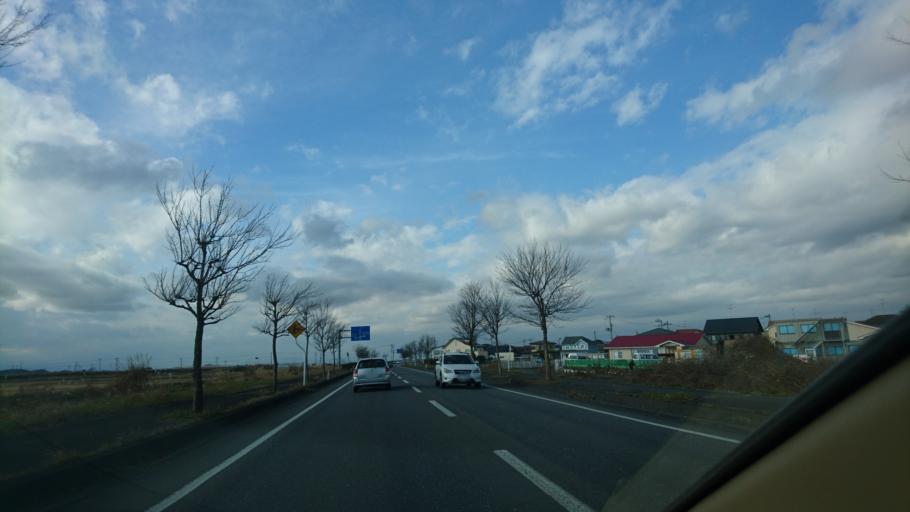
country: JP
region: Miyagi
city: Wakuya
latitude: 38.5322
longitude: 141.1259
